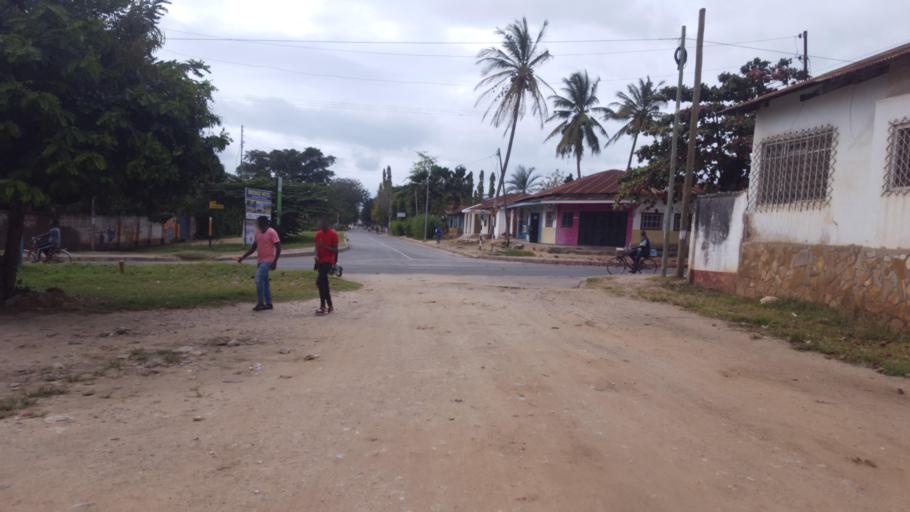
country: TZ
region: Tanga
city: Tanga
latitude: -5.0694
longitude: 39.0957
